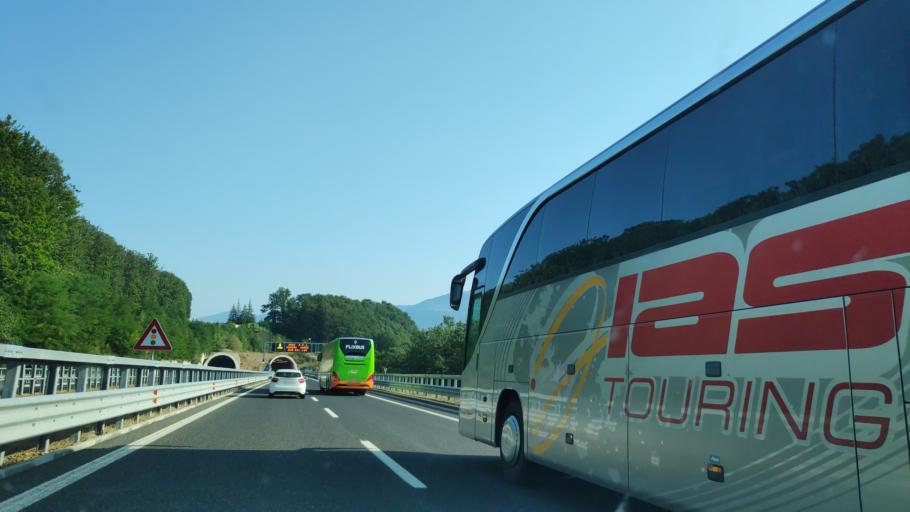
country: IT
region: Campania
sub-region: Provincia di Salerno
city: Buonabitacolo
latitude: 40.2496
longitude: 15.6602
